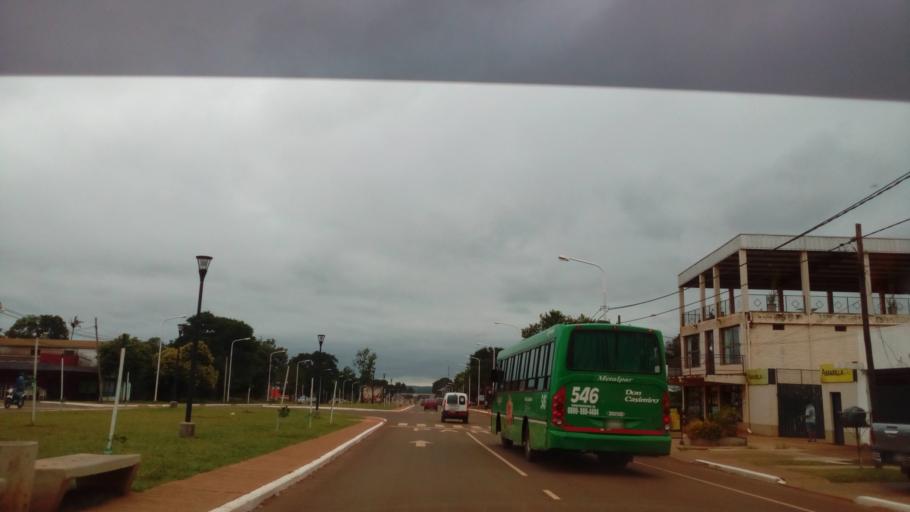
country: AR
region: Misiones
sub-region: Departamento de Candelaria
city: Candelaria
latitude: -27.4635
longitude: -55.7452
